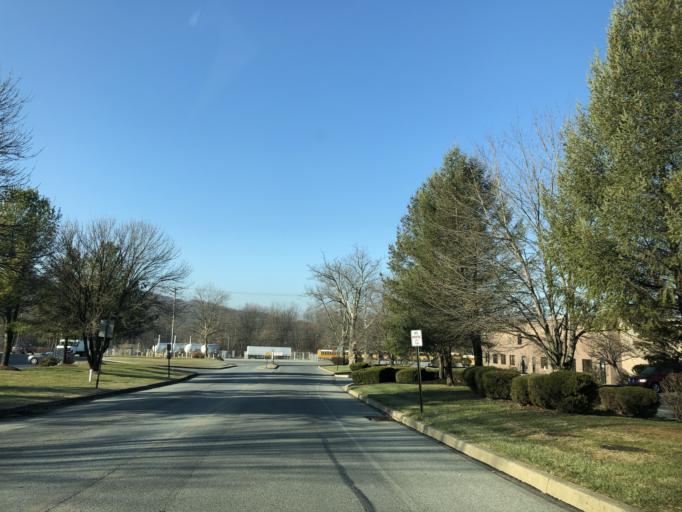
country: US
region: Pennsylvania
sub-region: Chester County
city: Downingtown
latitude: 39.9992
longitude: -75.7003
